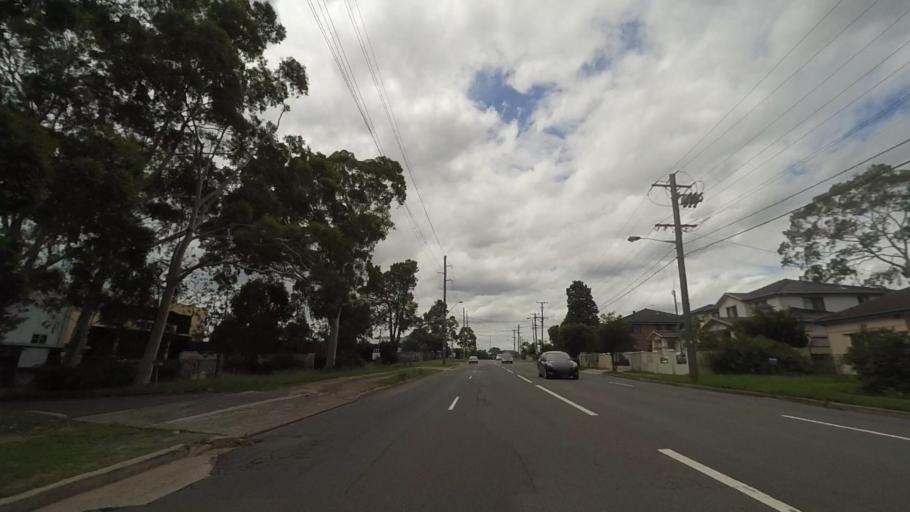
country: AU
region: New South Wales
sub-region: Holroyd
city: Guildford West
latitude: -33.8534
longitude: 150.9599
